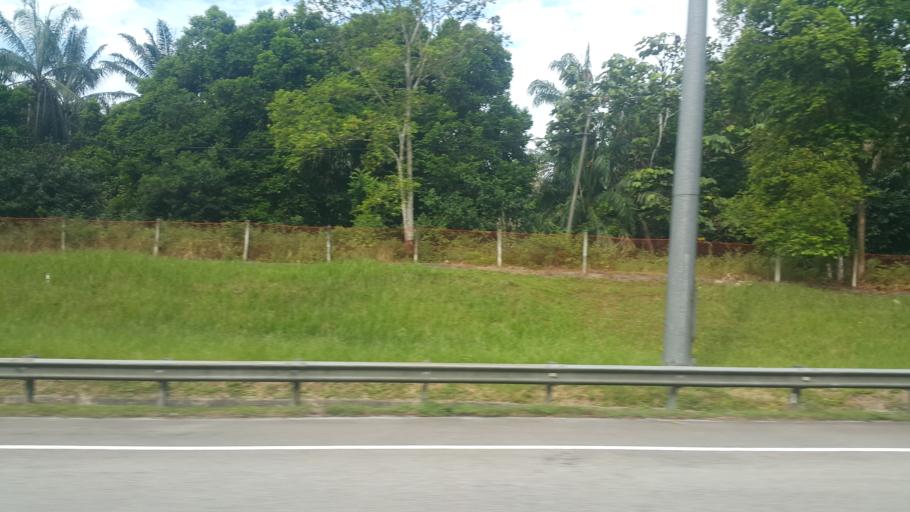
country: MY
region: Johor
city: Skudai
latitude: 1.5028
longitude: 103.6081
